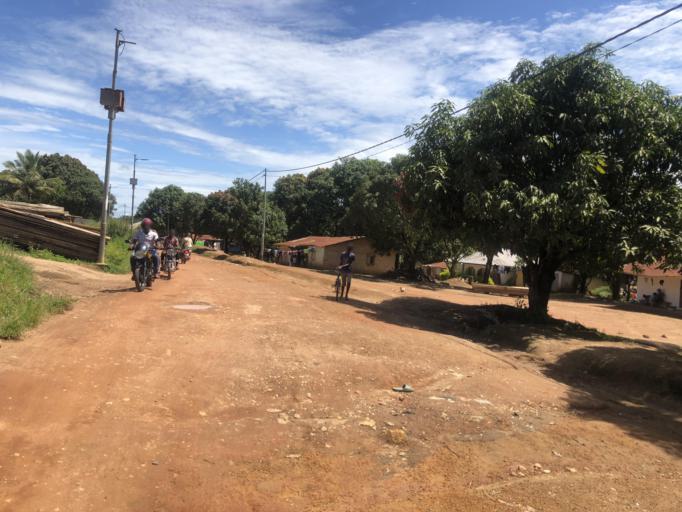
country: SL
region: Eastern Province
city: Koidu
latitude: 8.6402
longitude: -10.9550
